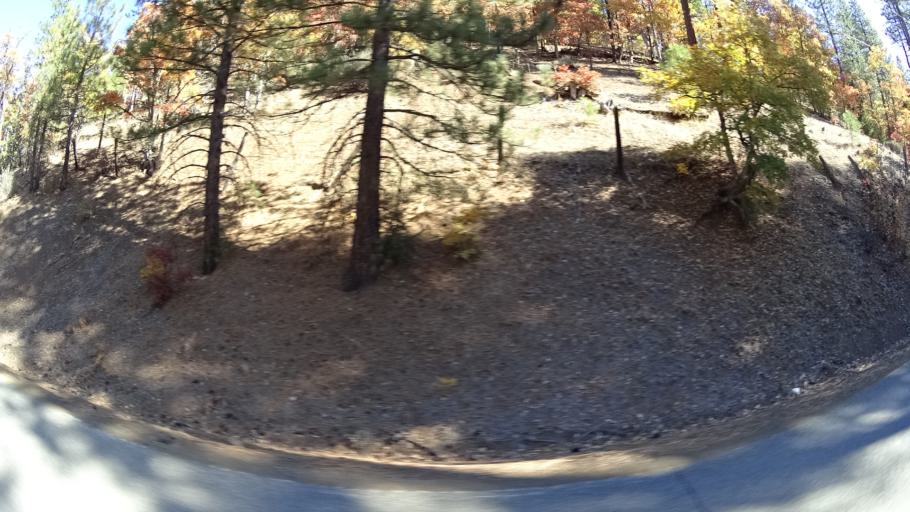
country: US
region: California
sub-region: Siskiyou County
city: Yreka
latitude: 41.6197
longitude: -122.9798
